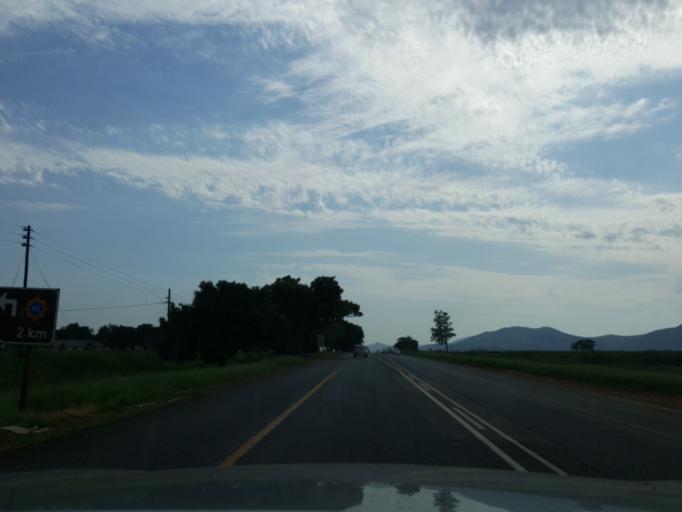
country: SZ
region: Hhohho
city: Ntfonjeni
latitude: -25.5065
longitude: 31.4893
